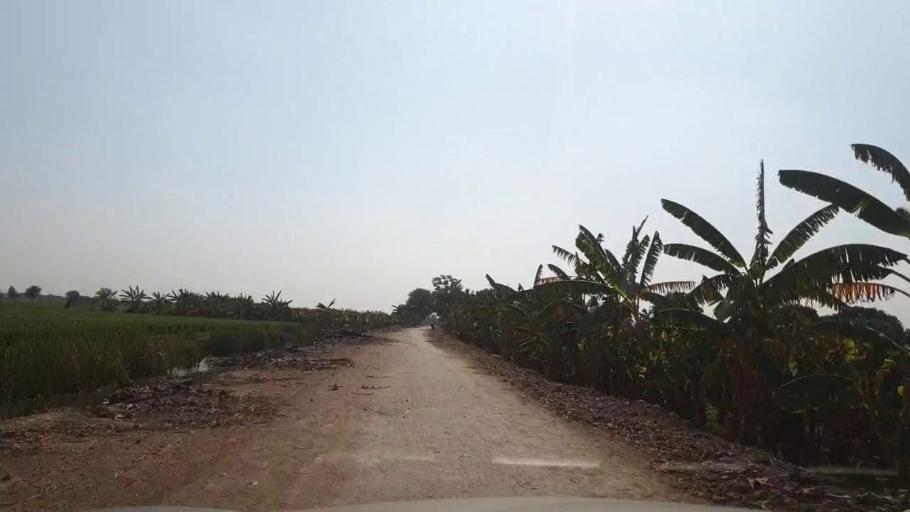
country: PK
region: Sindh
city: Tando Allahyar
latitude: 25.5497
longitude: 68.6982
